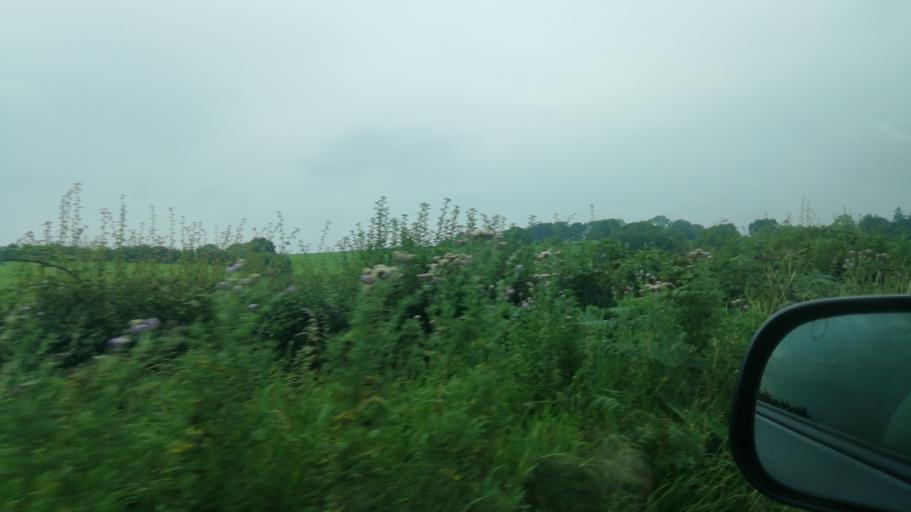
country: IE
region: Munster
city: Fethard
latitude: 52.5788
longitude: -7.6388
